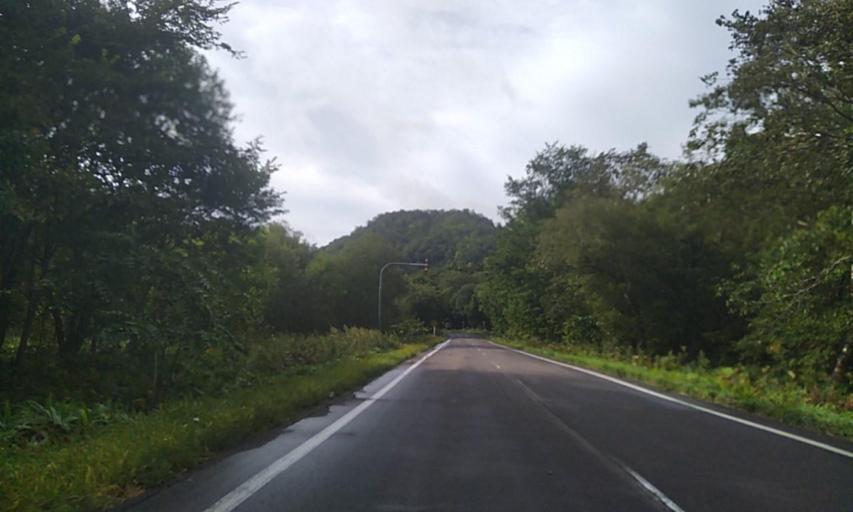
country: JP
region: Hokkaido
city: Abashiri
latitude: 43.6759
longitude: 144.5485
